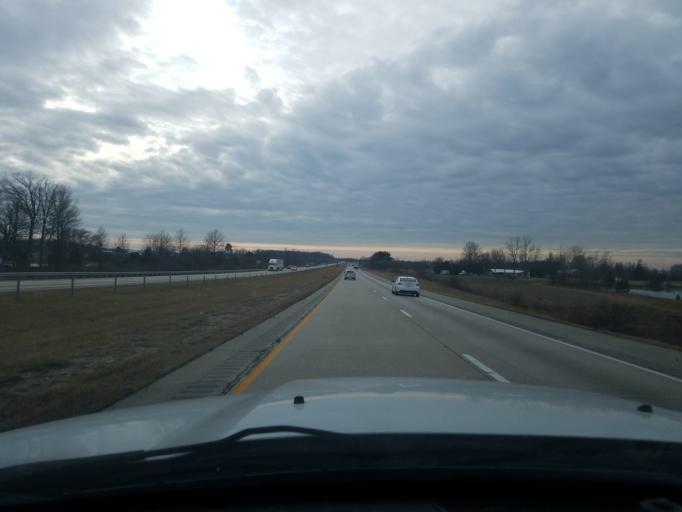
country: US
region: Indiana
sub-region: Huntington County
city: Warren
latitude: 40.6138
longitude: -85.5339
